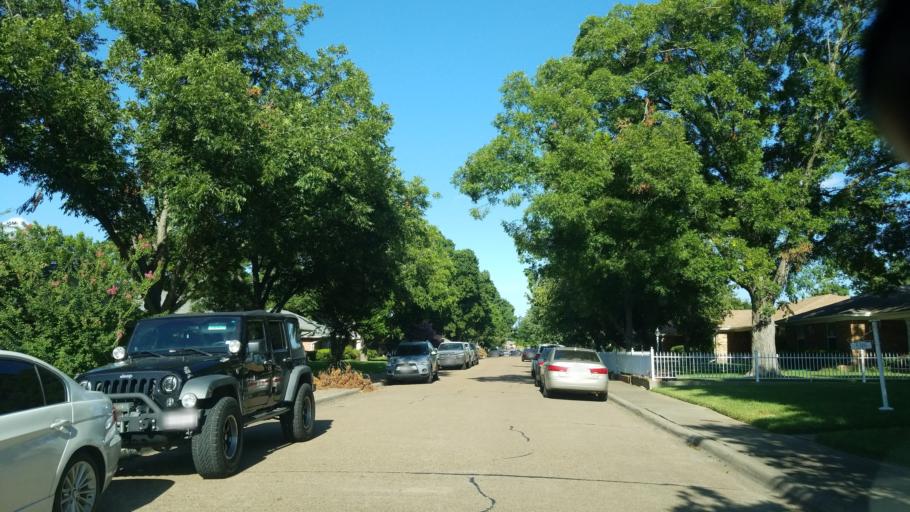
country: US
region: Texas
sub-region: Dallas County
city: Highland Park
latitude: 32.7915
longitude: -96.7074
